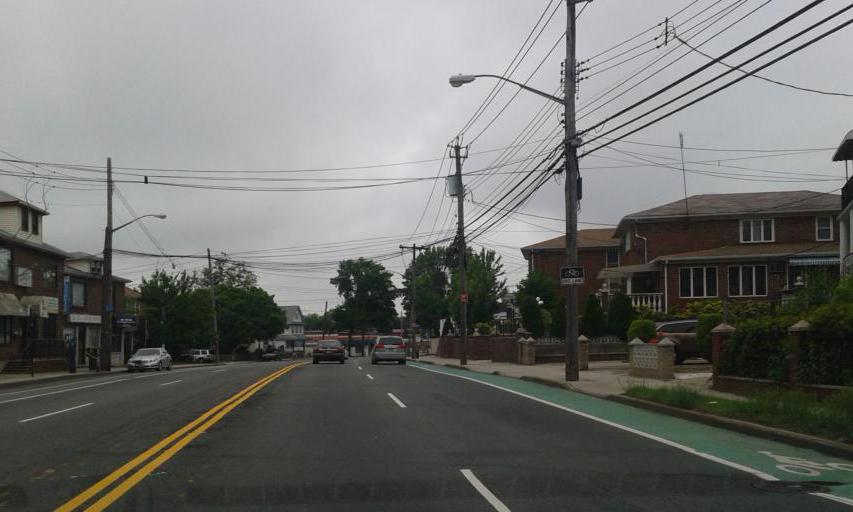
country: US
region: New Jersey
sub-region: Hudson County
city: Bayonne
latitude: 40.6139
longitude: -74.1010
